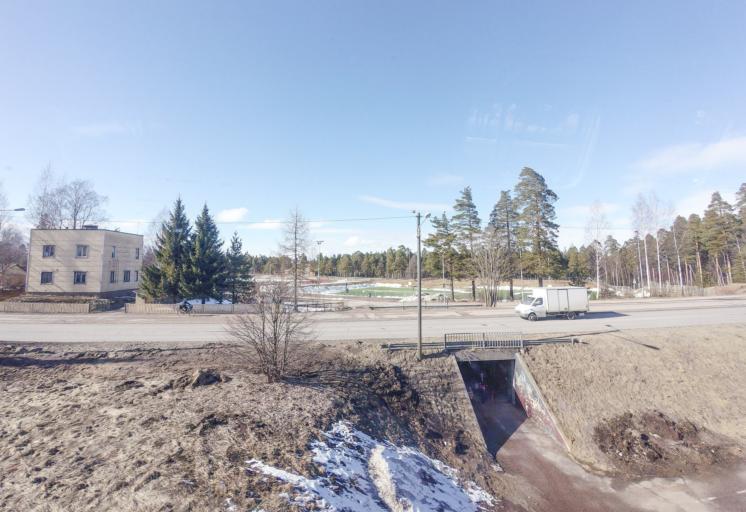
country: FI
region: South Karelia
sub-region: Lappeenranta
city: Lappeenranta
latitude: 61.0737
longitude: 28.2701
